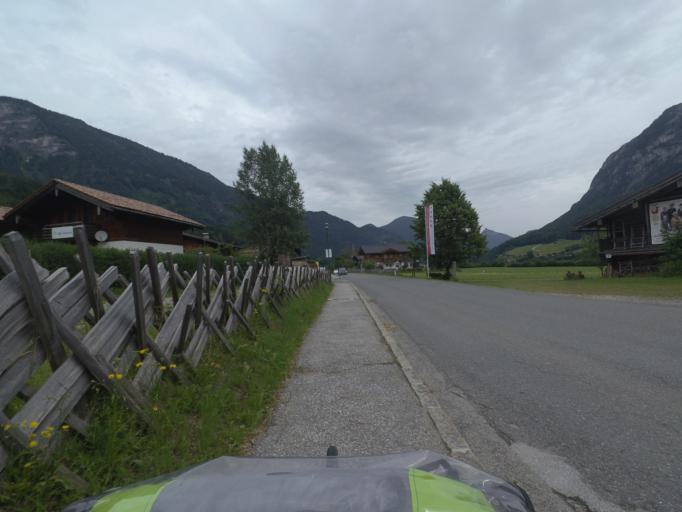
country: AT
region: Salzburg
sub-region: Politischer Bezirk Zell am See
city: Unken
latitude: 47.6466
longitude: 12.7240
